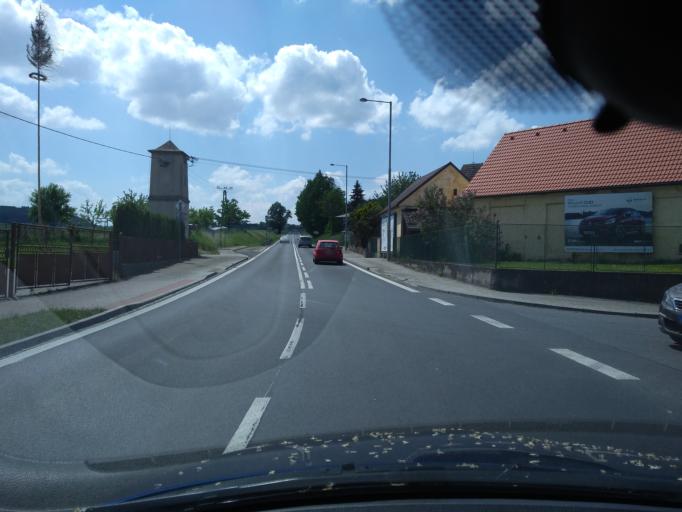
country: CZ
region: Plzensky
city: Svihov
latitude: 49.4478
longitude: 13.2874
